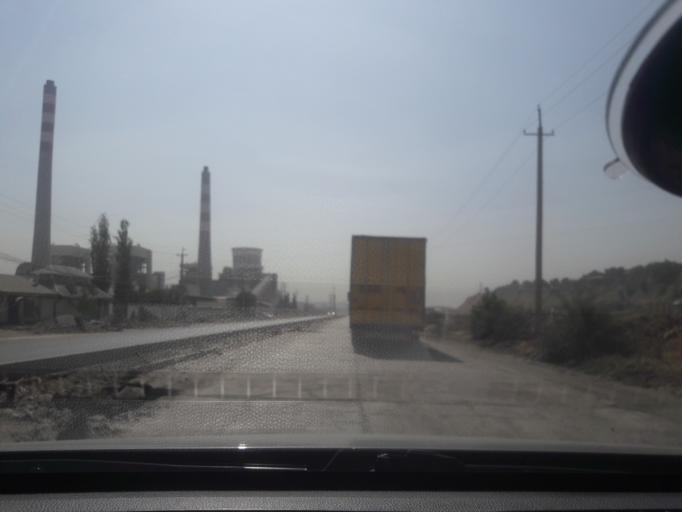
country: TJ
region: Dushanbe
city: Dushanbe
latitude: 38.6145
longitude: 68.7691
